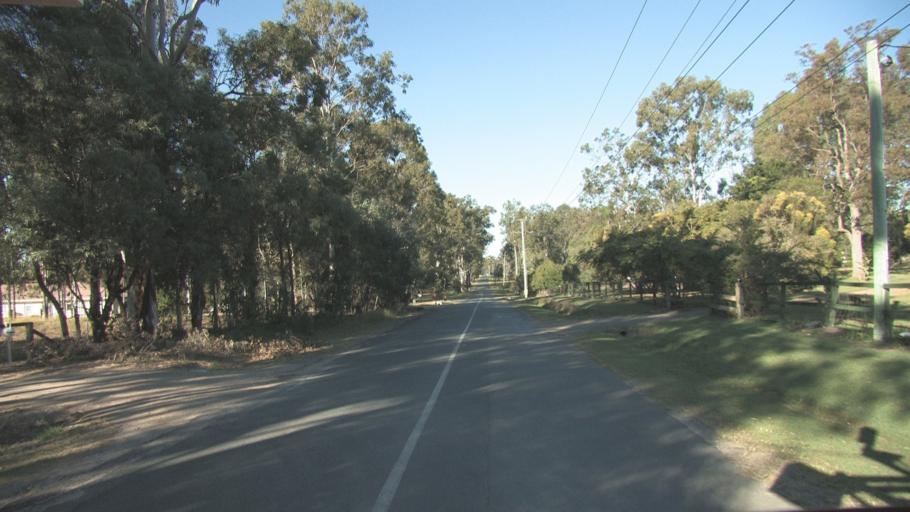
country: AU
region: Queensland
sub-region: Logan
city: Logan Reserve
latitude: -27.7411
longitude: 153.1044
